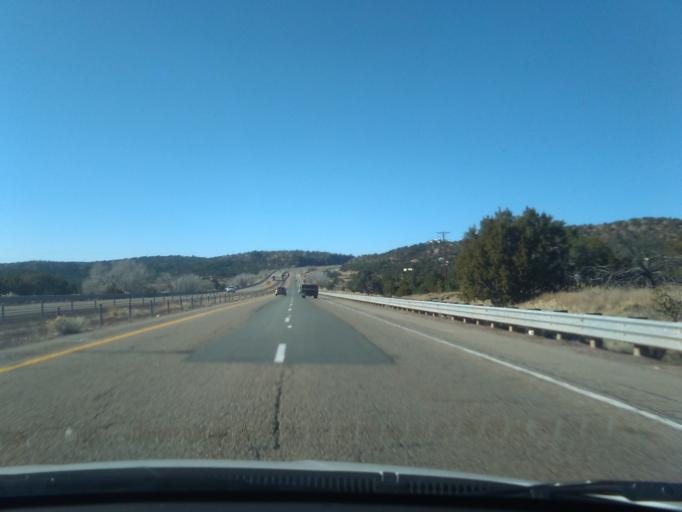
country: US
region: New Mexico
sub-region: Santa Fe County
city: Eldorado at Santa Fe
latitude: 35.5419
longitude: -105.8413
